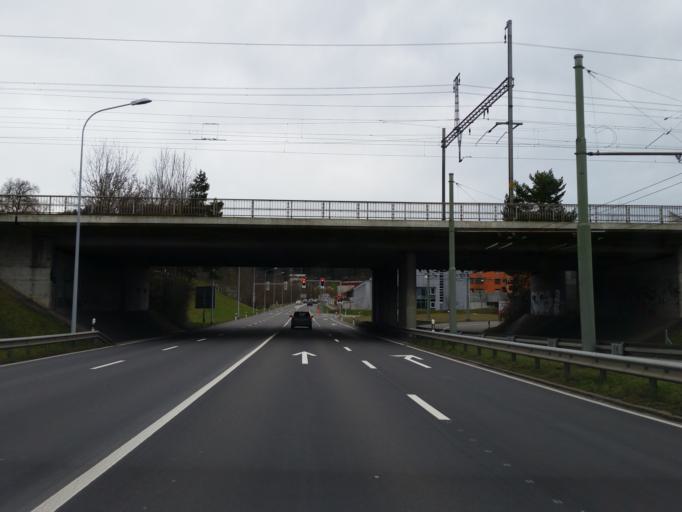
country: CH
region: Appenzell Ausserrhoden
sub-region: Bezirk Hinterland
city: Herisau
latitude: 47.4036
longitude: 9.3049
